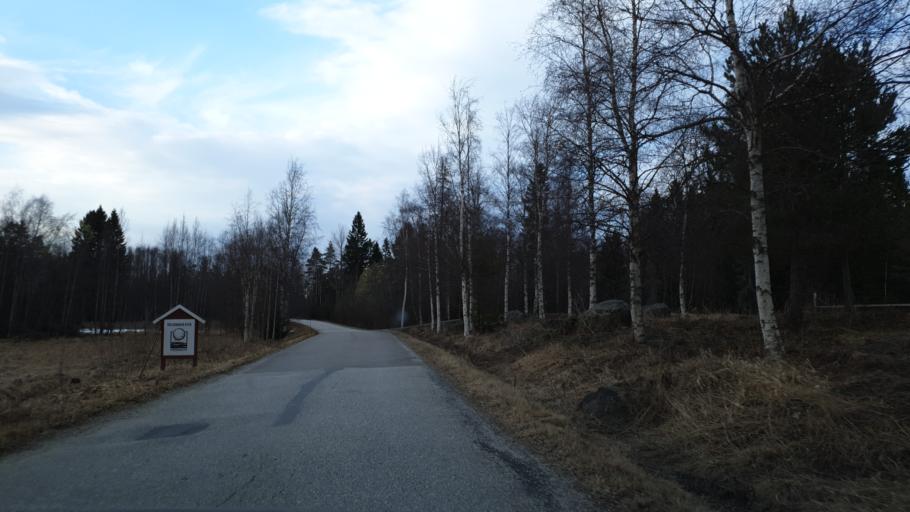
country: SE
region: Vaesternorrland
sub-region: Sundsvalls Kommun
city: Njurundabommen
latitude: 62.0213
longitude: 17.4073
